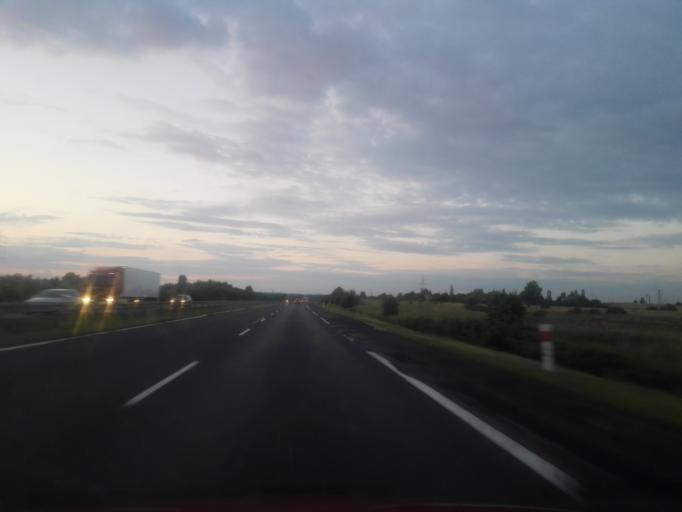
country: PL
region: Lodz Voivodeship
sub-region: Powiat radomszczanski
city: Kamiensk
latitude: 51.1990
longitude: 19.4765
